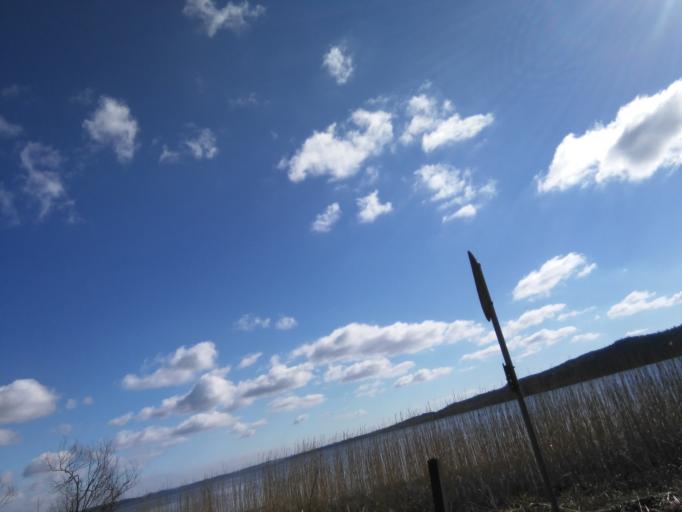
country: DK
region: Central Jutland
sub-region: Skanderborg Kommune
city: Ry
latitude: 56.0424
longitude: 9.7086
